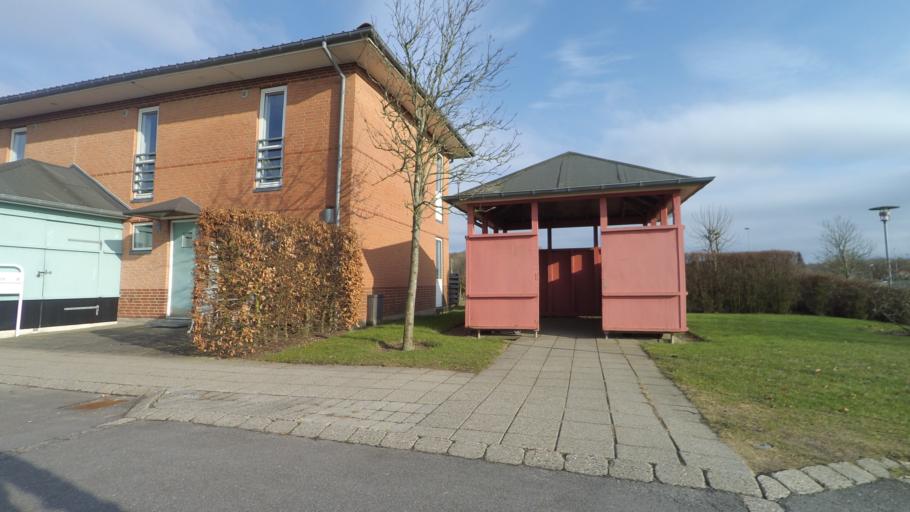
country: DK
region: Central Jutland
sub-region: Arhus Kommune
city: Kolt
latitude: 56.1105
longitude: 10.0824
